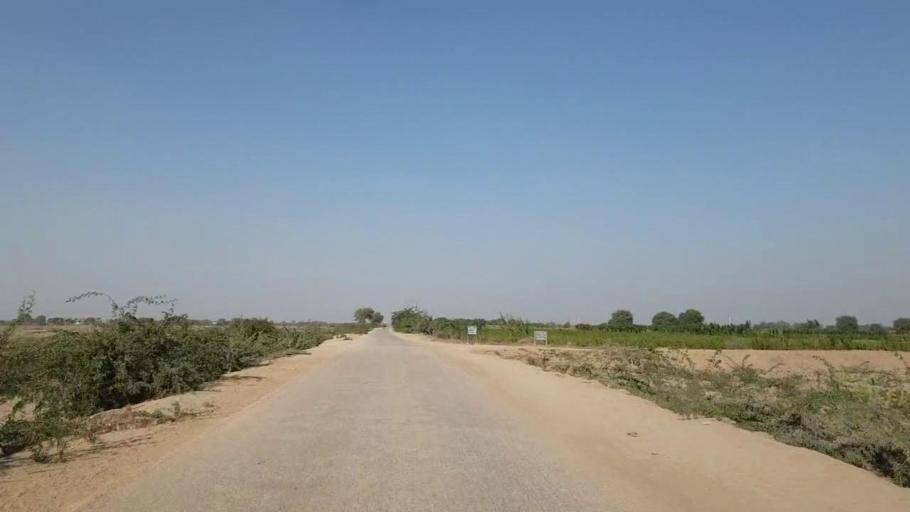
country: PK
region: Sindh
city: Digri
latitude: 25.0153
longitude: 69.1061
